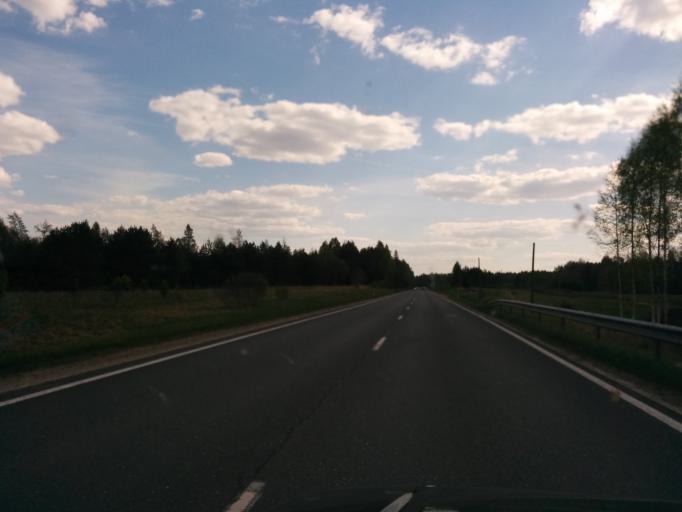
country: LV
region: Pargaujas
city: Stalbe
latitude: 57.3255
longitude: 24.9221
